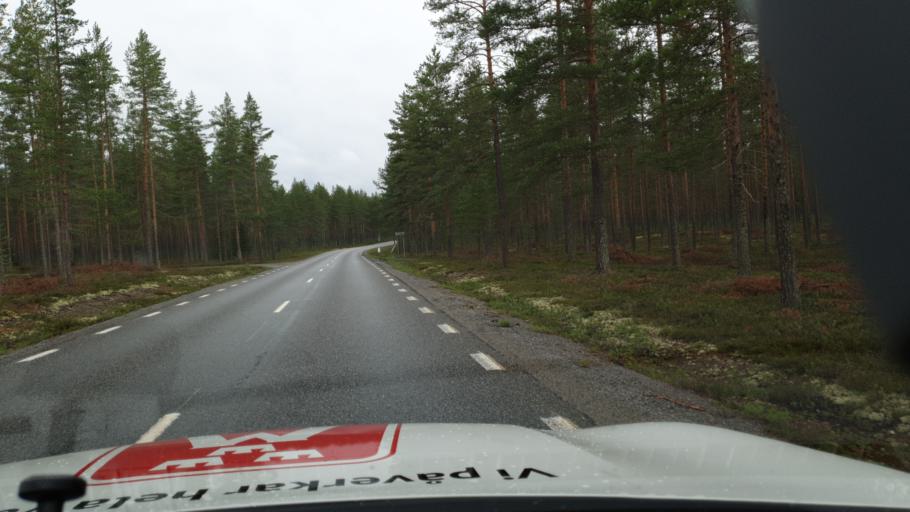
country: SE
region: Vaesterbotten
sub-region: Umea Kommun
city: Saevar
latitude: 63.9907
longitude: 20.4980
